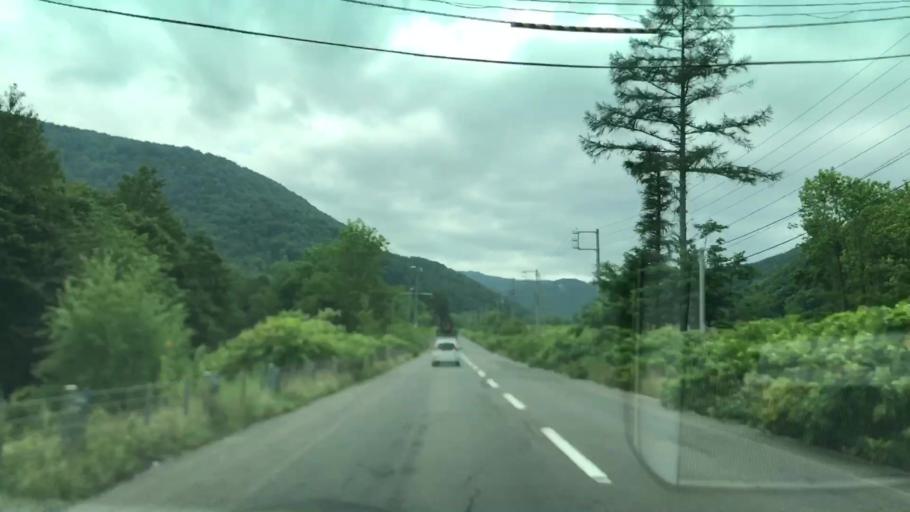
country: JP
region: Hokkaido
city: Yoichi
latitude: 43.0346
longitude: 140.8639
